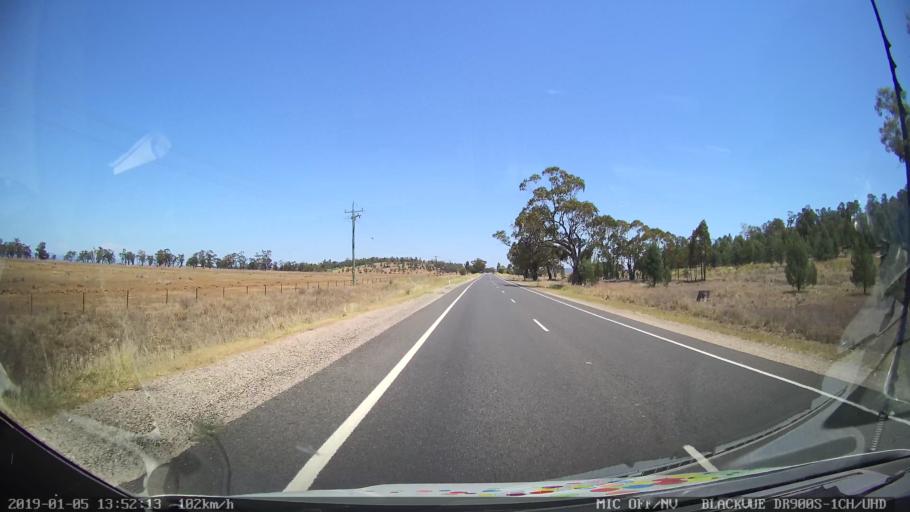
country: AU
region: New South Wales
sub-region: Gunnedah
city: Gunnedah
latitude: -31.0564
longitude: 150.2778
